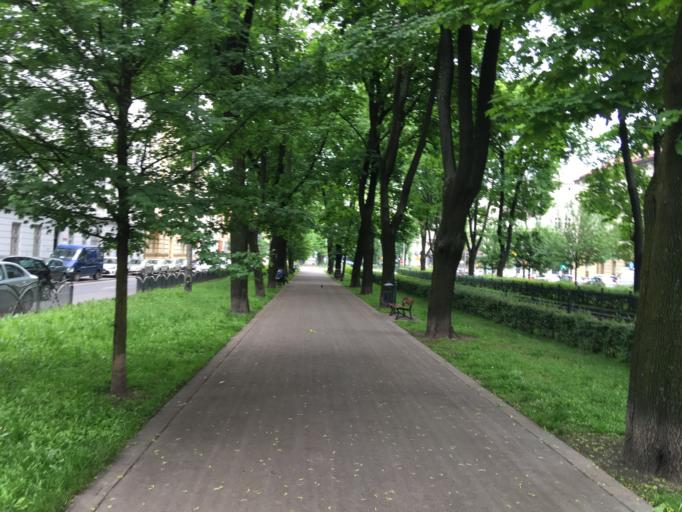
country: PL
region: Lesser Poland Voivodeship
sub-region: Krakow
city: Krakow
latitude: 50.0543
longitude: 19.9437
